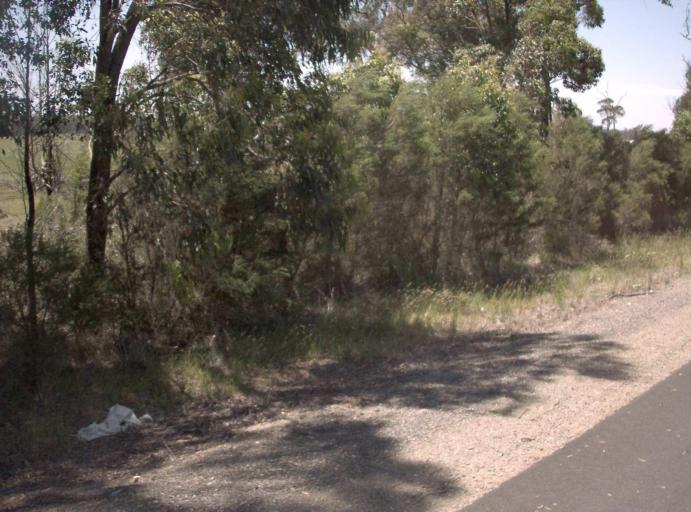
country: AU
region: Victoria
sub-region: East Gippsland
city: Lakes Entrance
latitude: -37.7554
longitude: 148.3086
